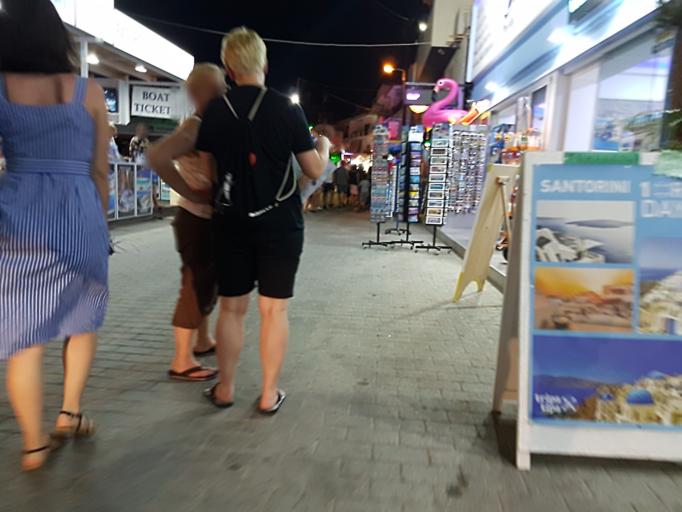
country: GR
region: Crete
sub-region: Nomos Irakleiou
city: Limin Khersonisou
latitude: 35.3224
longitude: 25.3918
